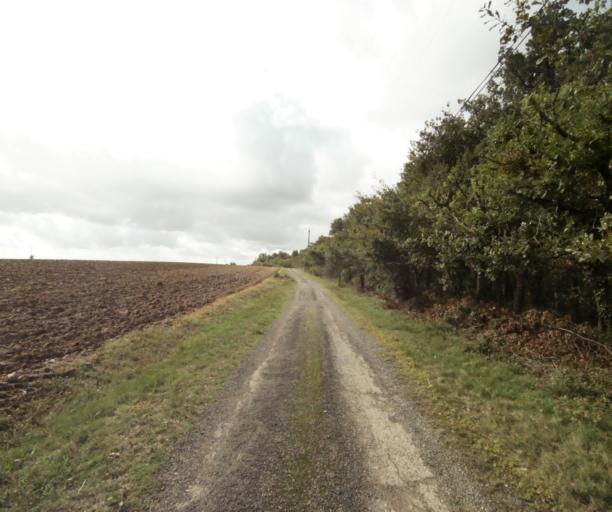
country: FR
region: Midi-Pyrenees
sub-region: Departement du Tarn-et-Garonne
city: Beaumont-de-Lomagne
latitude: 43.8812
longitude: 1.0743
